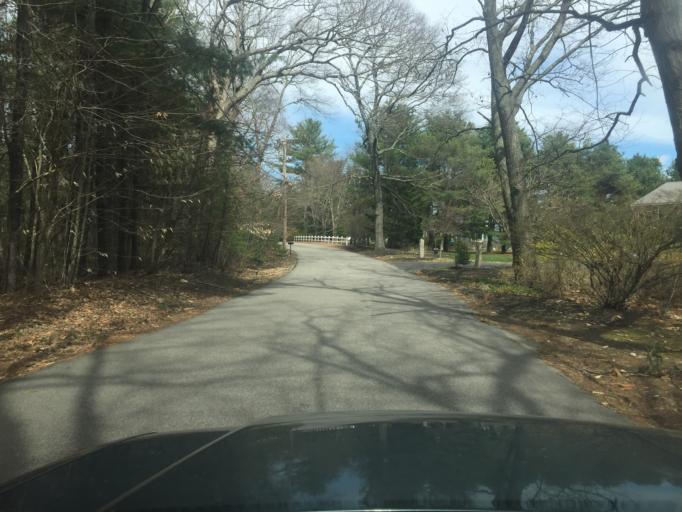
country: US
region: Massachusetts
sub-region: Norfolk County
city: Medway
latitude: 42.1774
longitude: -71.3971
